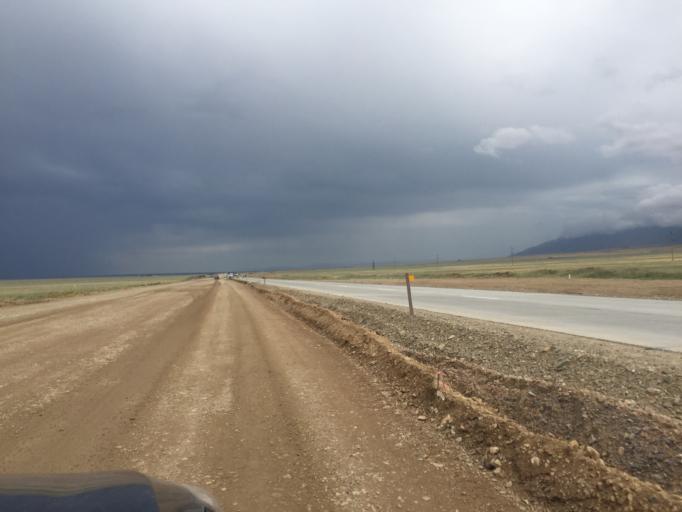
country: KG
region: Chuy
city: Ivanovka
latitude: 43.3773
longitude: 75.2369
